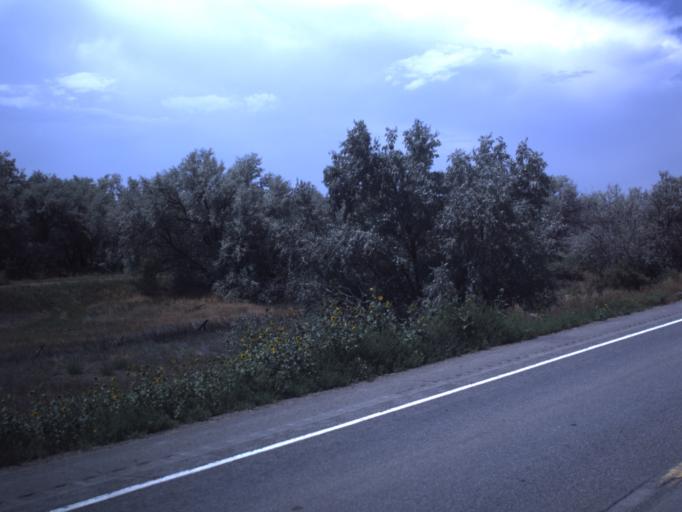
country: US
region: Utah
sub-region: Duchesne County
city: Roosevelt
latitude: 40.3025
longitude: -109.7938
